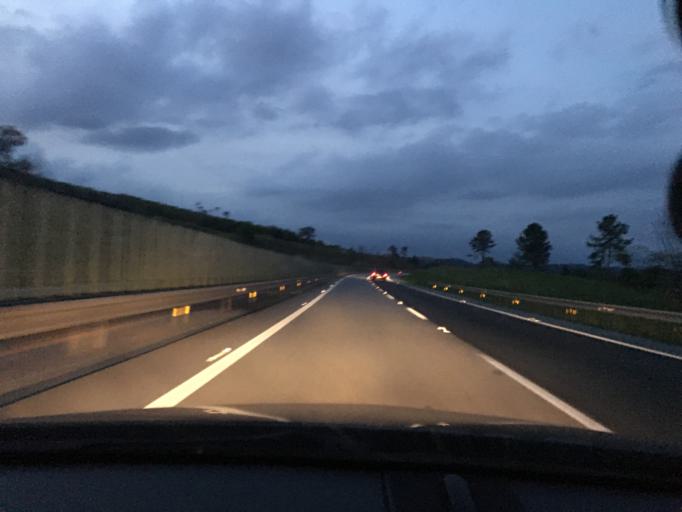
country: BR
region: Sao Paulo
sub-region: Santa Isabel
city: Santa Isabel
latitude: -23.3521
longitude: -46.1255
